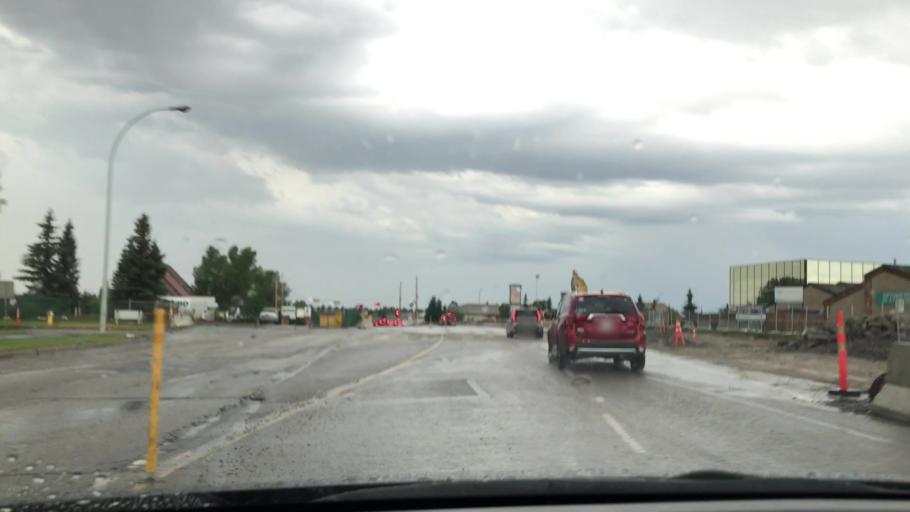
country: CA
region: Alberta
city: Edmonton
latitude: 53.4604
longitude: -113.4343
